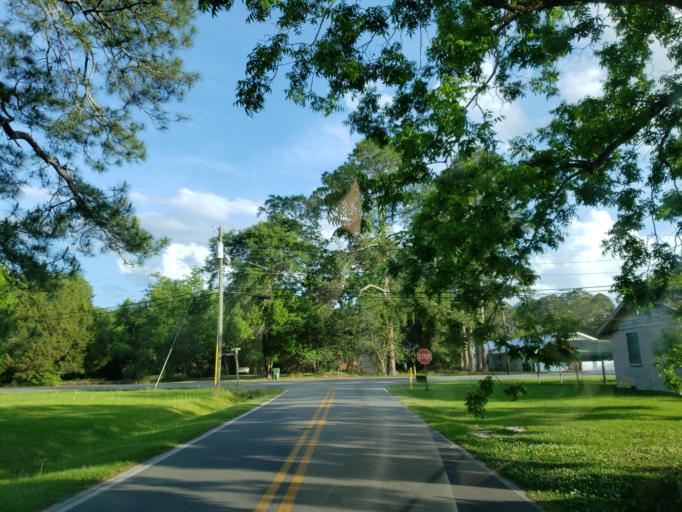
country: US
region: Georgia
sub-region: Cook County
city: Adel
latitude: 31.1340
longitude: -83.4313
